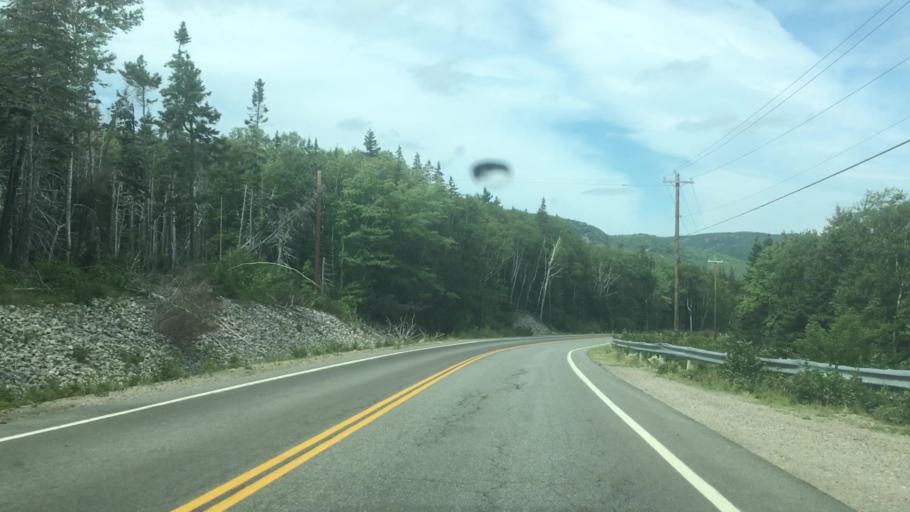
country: CA
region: Nova Scotia
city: Sydney Mines
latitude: 46.5384
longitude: -60.4138
